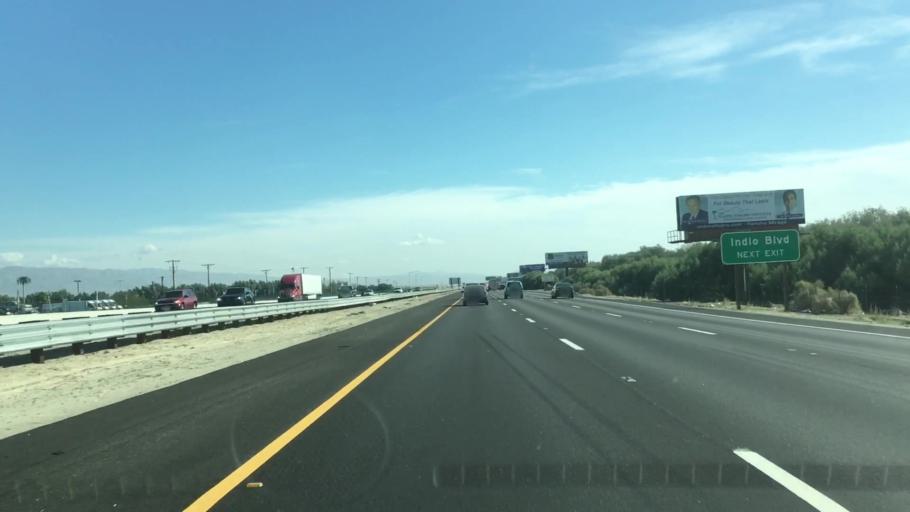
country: US
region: California
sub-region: Riverside County
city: Bermuda Dunes
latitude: 33.7544
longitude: -116.2841
